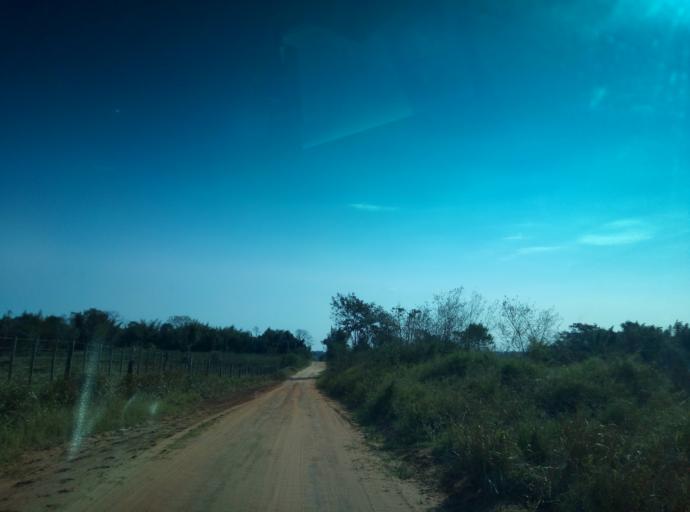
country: PY
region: Caaguazu
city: Doctor Cecilio Baez
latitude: -25.1649
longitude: -56.2135
